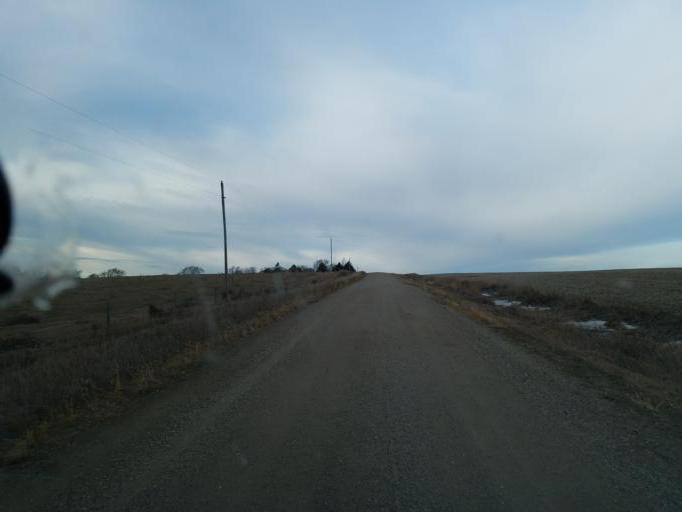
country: US
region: Nebraska
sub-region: Knox County
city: Bloomfield
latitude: 42.5833
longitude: -97.6265
